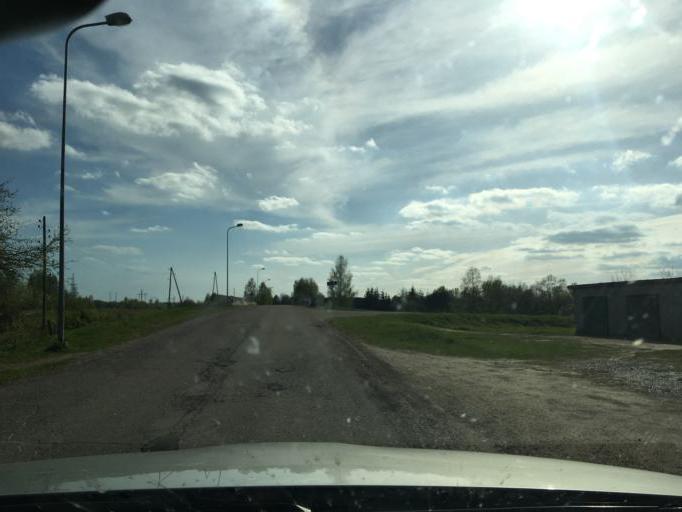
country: LV
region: Ozolnieku
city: Ozolnieki
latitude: 56.6833
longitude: 23.8450
